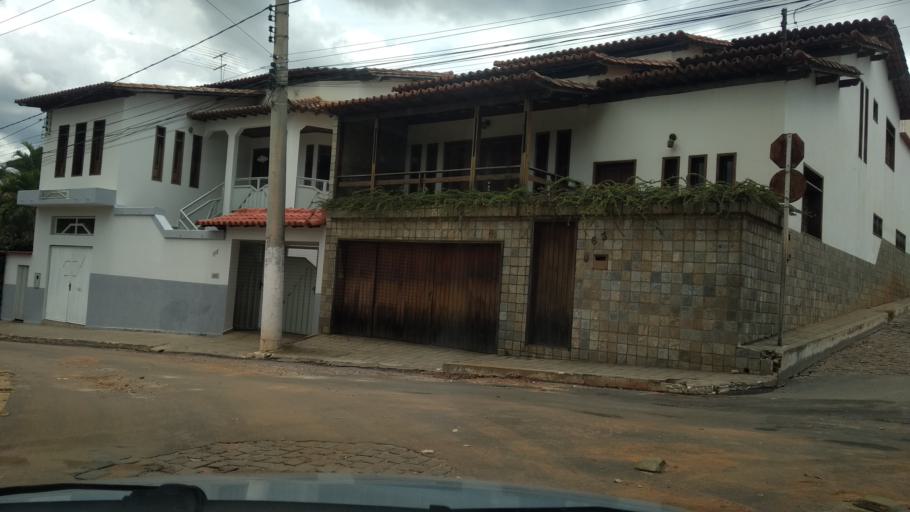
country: BR
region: Bahia
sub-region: Caetite
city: Caetite
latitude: -14.0708
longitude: -42.4917
